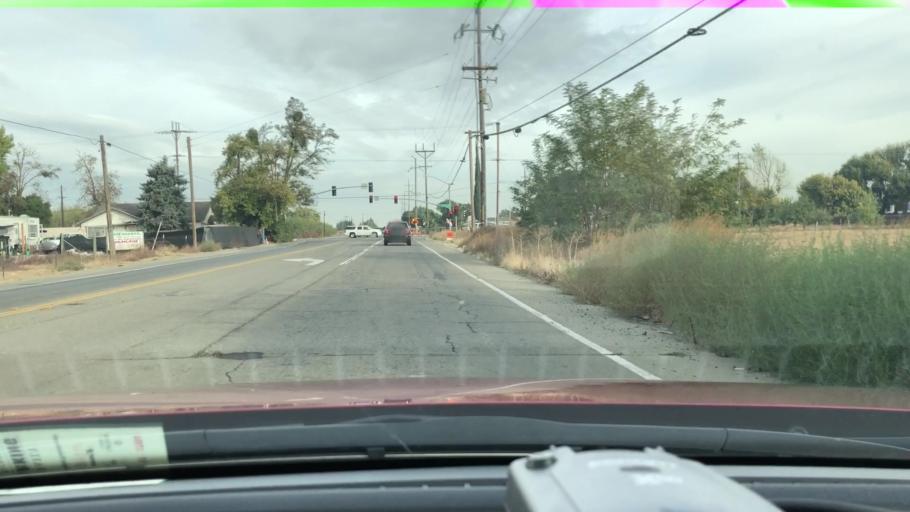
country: US
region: California
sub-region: San Joaquin County
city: Lathrop
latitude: 37.8253
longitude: -121.2537
